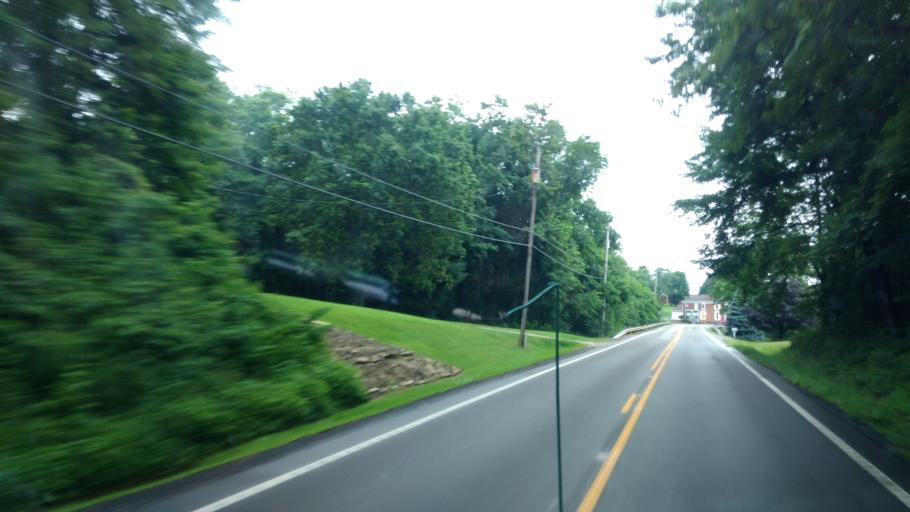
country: US
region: Ohio
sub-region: Stark County
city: Minerva
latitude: 40.6846
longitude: -81.0237
